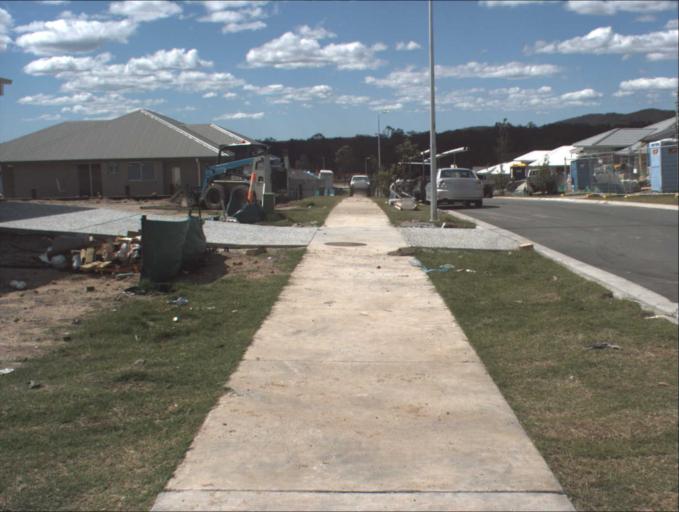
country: AU
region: Queensland
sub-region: Logan
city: Chambers Flat
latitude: -27.8024
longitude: 153.1150
